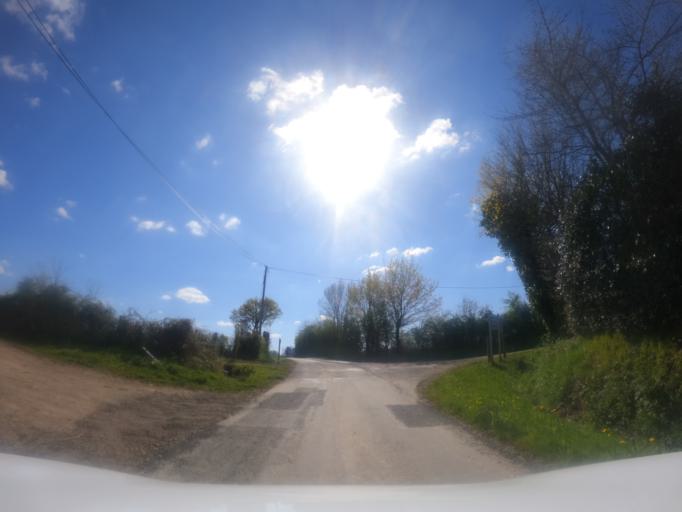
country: FR
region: Pays de la Loire
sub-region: Departement de la Vendee
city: Saint-Vincent-sur-Graon
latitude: 46.5309
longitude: -1.3764
